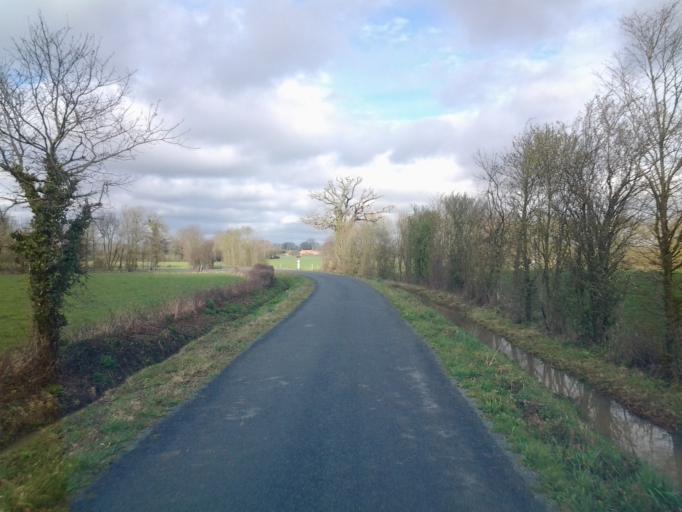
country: FR
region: Pays de la Loire
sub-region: Departement de la Vendee
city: La Chaize-le-Vicomte
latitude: 46.6530
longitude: -1.3571
